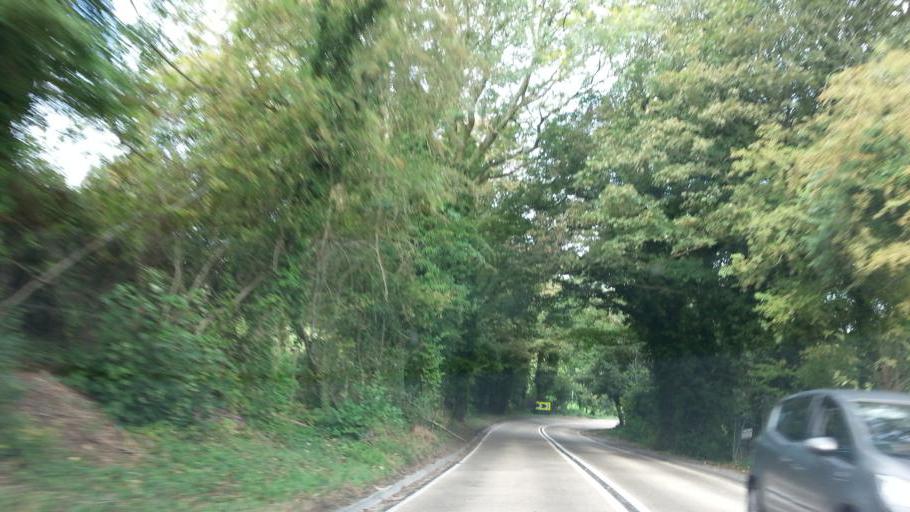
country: GB
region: England
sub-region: Gloucestershire
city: Stroud
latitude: 51.7619
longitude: -2.2221
